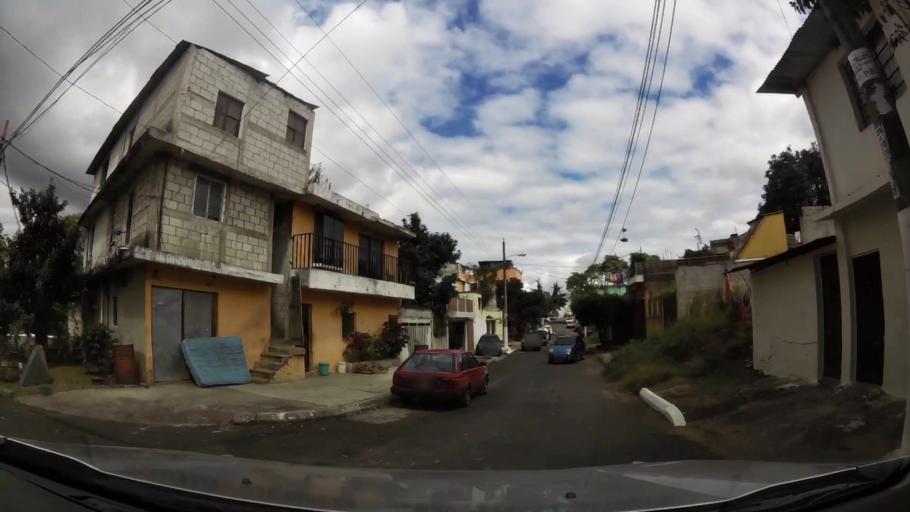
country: GT
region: Guatemala
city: Chinautla
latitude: 14.6871
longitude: -90.5512
